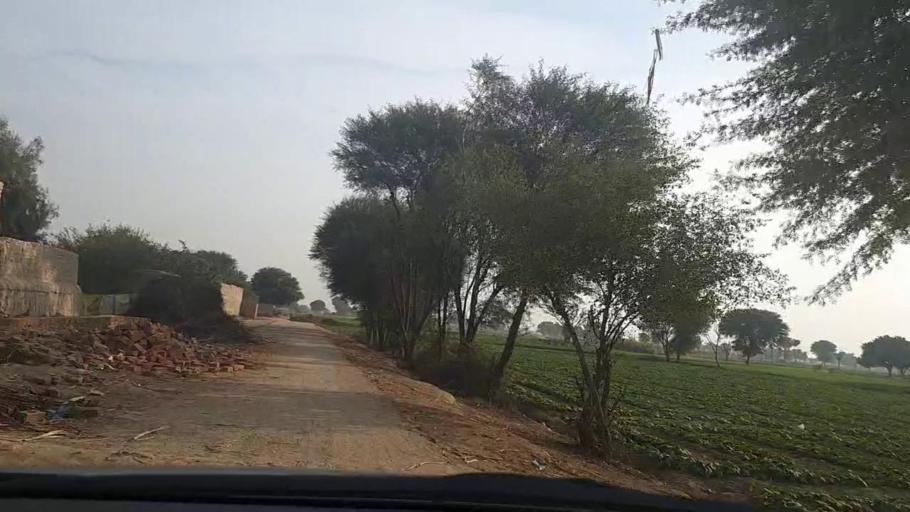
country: PK
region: Sindh
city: Daulatpur
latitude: 26.3314
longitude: 68.0550
